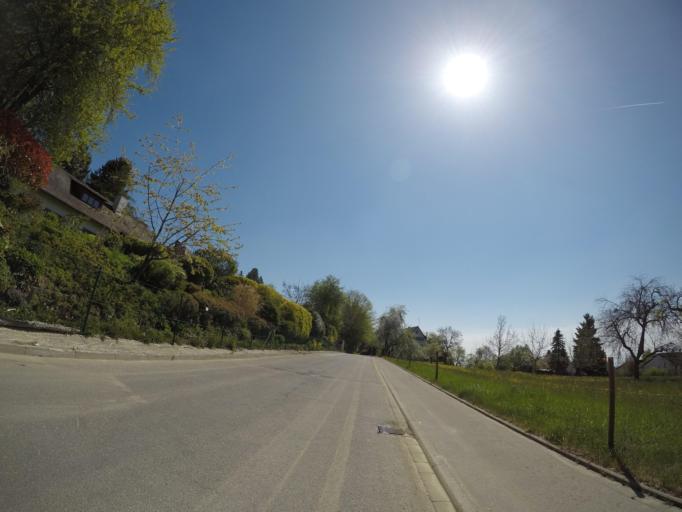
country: DE
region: Baden-Wuerttemberg
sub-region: Tuebingen Region
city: Markdorf
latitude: 47.7363
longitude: 9.3837
